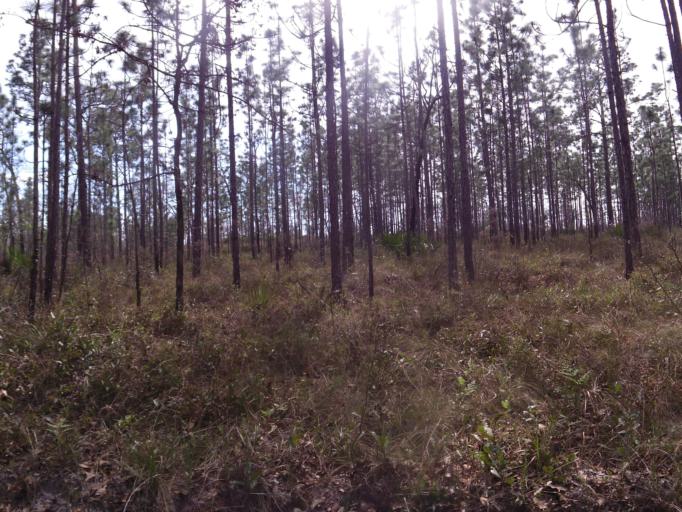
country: US
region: Florida
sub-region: Clay County
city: Middleburg
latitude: 30.1262
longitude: -81.8882
